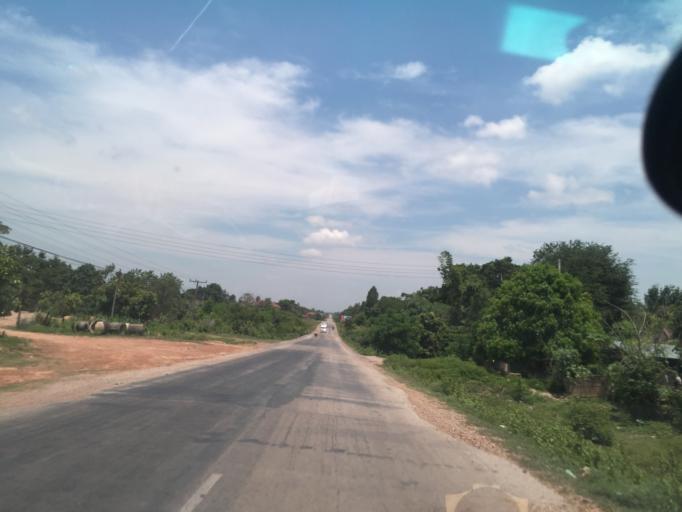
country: TH
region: Mukdahan
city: Don Tan
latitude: 16.4927
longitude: 105.0290
